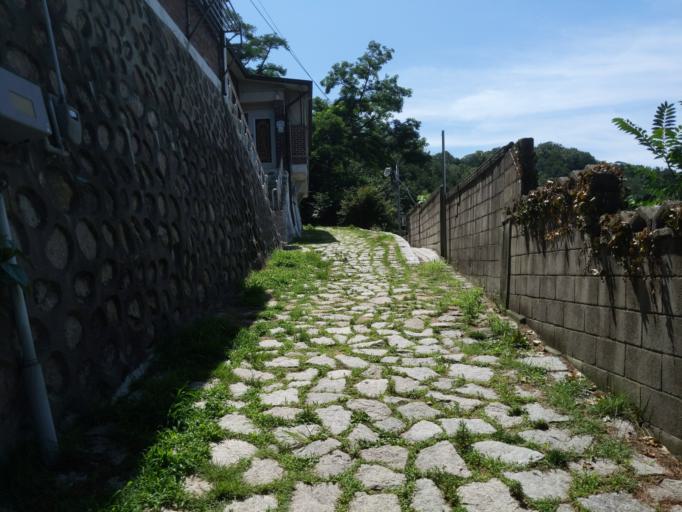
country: KR
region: Seoul
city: Seoul
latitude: 37.6019
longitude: 126.9632
